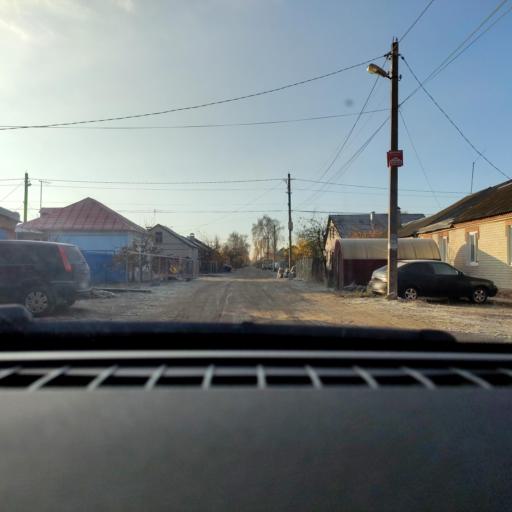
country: RU
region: Voronezj
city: Somovo
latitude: 51.7417
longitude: 39.2771
